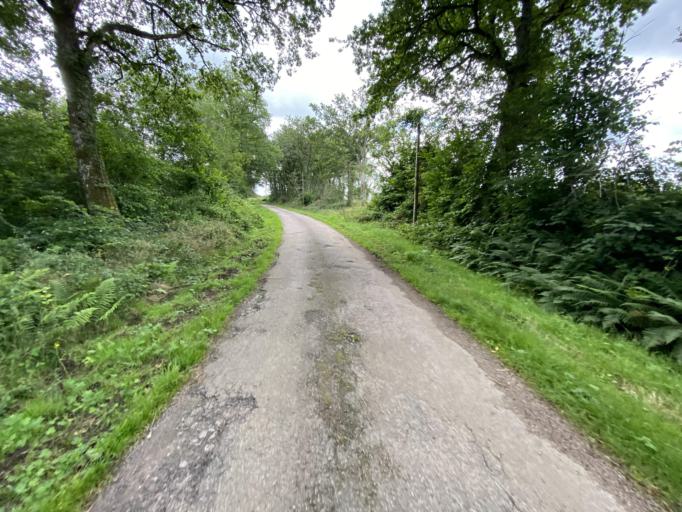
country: FR
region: Bourgogne
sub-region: Departement de la Cote-d'Or
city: Saulieu
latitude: 47.2846
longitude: 4.1738
